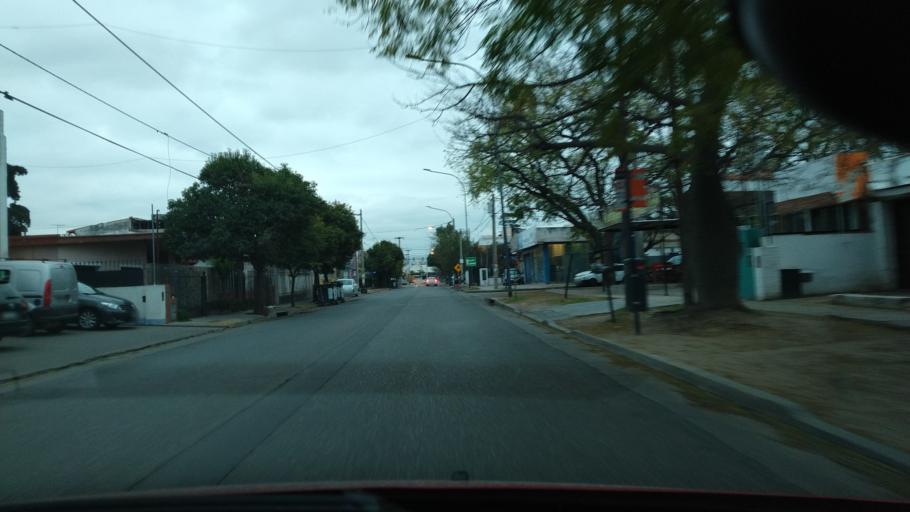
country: AR
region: Cordoba
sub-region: Departamento de Capital
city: Cordoba
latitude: -31.3589
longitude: -64.2369
